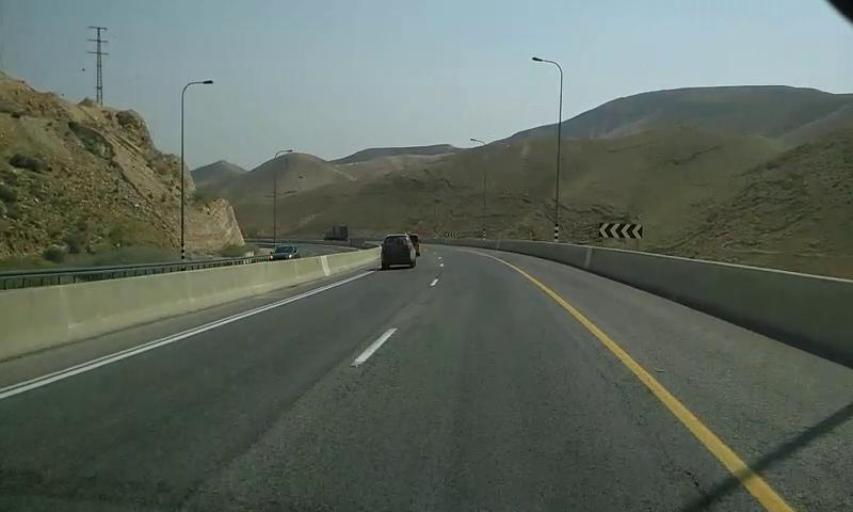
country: PS
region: West Bank
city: Jericho
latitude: 31.8106
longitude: 35.3907
